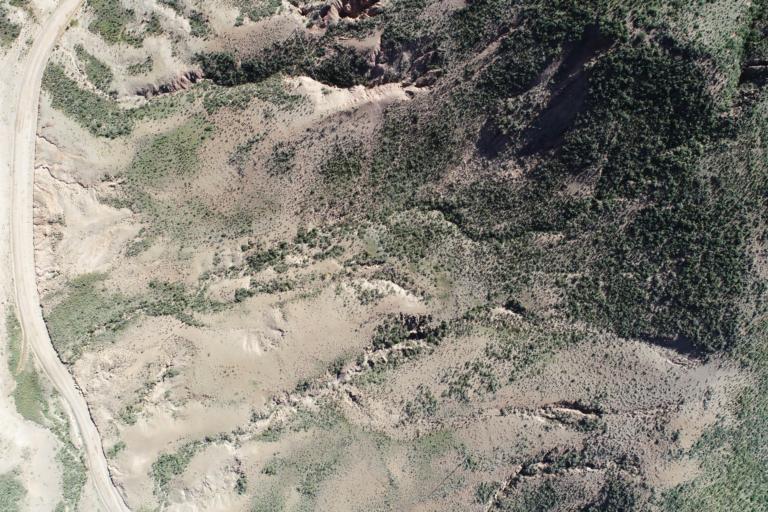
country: BO
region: La Paz
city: Curahuara de Carangas
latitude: -17.3037
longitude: -68.4919
